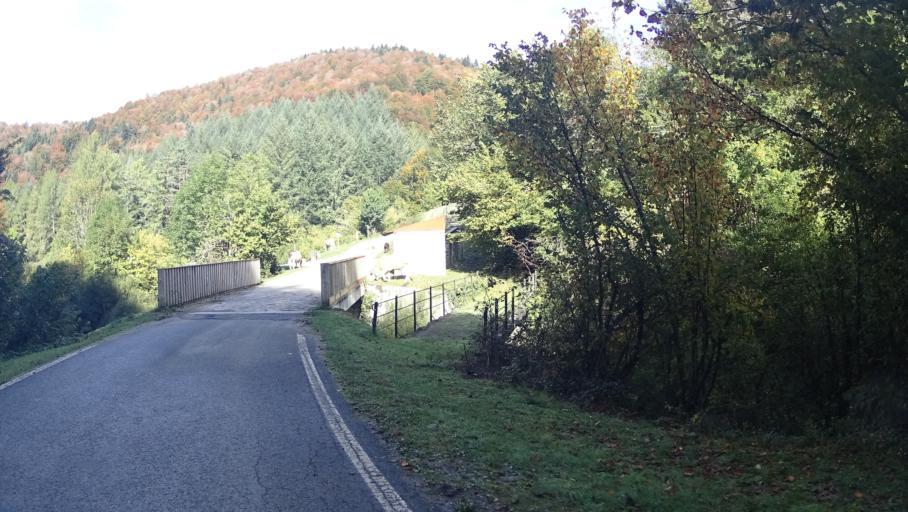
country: ES
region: Navarre
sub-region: Provincia de Navarra
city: Oronz
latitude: 42.9882
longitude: -1.1053
